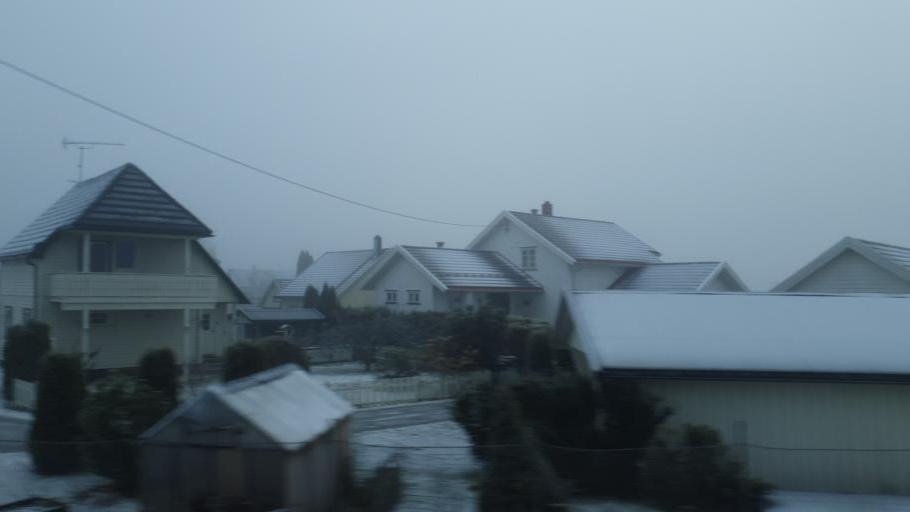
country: NO
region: Buskerud
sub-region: Lier
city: Lierbyen
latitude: 59.7577
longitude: 10.2708
